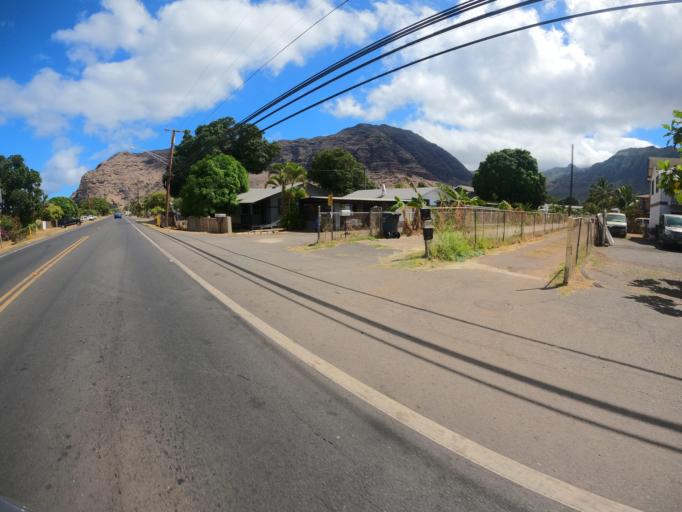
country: US
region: Hawaii
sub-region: Honolulu County
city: Makaha
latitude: 21.4687
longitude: -158.2151
